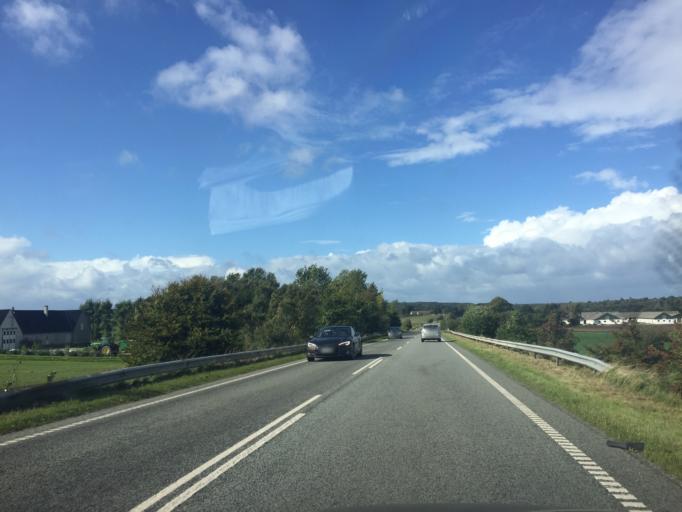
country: DK
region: Capital Region
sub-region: Gribskov Kommune
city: Helsinge
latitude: 56.0377
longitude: 12.1486
